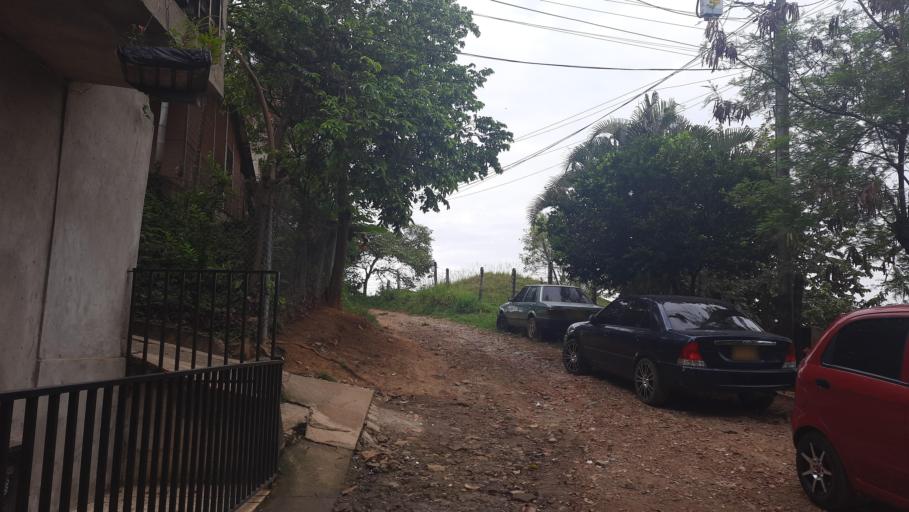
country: CO
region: Valle del Cauca
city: Cali
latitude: 3.3739
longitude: -76.5597
